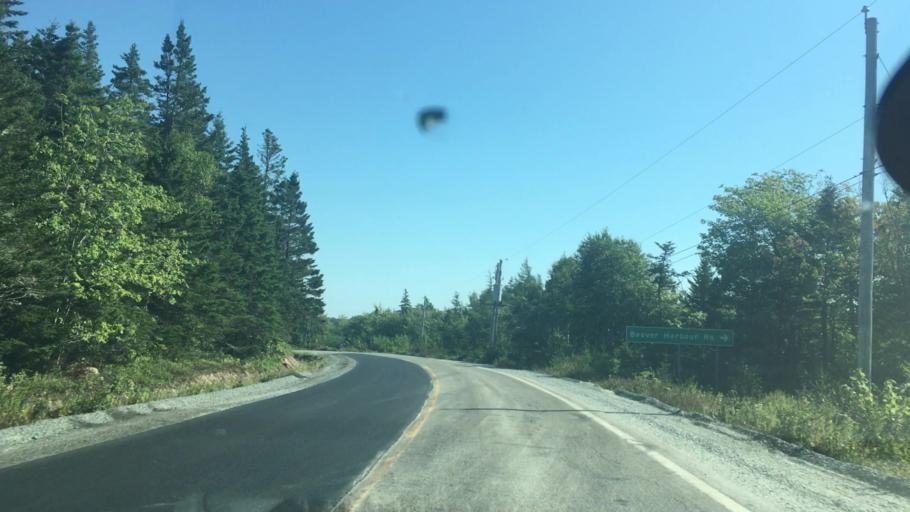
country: CA
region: Nova Scotia
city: New Glasgow
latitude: 44.8983
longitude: -62.4217
